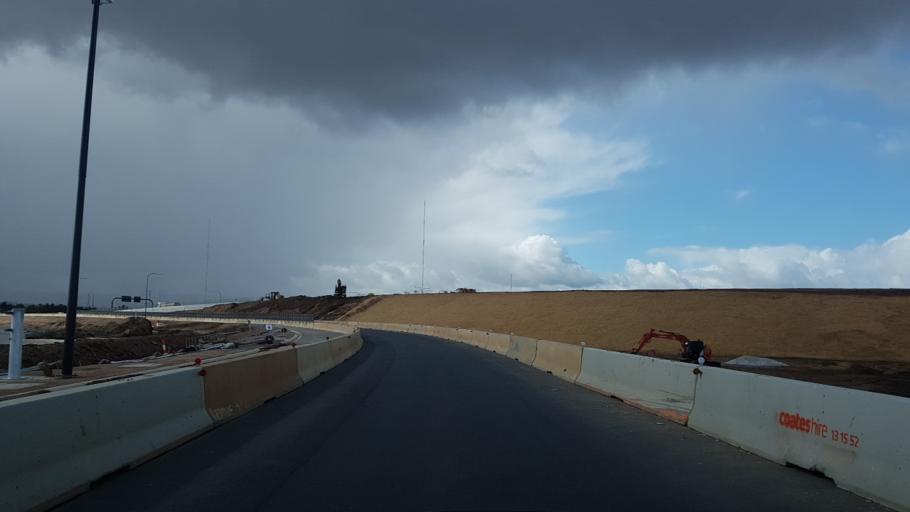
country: AU
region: South Australia
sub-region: Port Adelaide Enfield
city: Blair Athol
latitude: -34.8304
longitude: 138.5669
